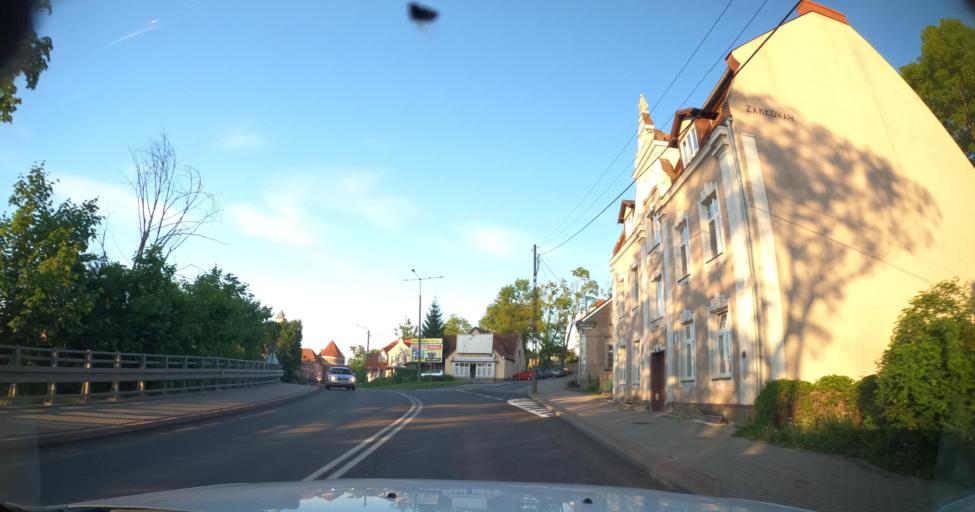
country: PL
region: Warmian-Masurian Voivodeship
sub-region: Powiat lidzbarski
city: Lidzbark Warminski
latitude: 54.1236
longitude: 20.5811
